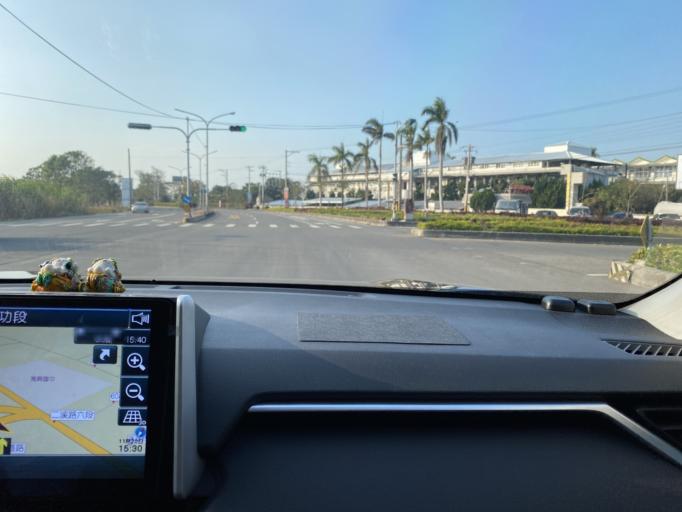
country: TW
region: Taiwan
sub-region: Changhua
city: Chang-hua
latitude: 23.9548
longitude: 120.4158
